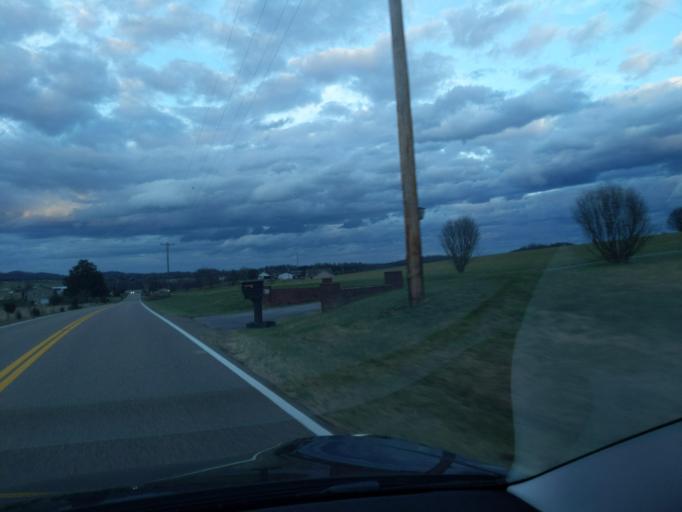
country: US
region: Tennessee
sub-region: Jefferson County
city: Dandridge
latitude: 36.0746
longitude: -83.3827
